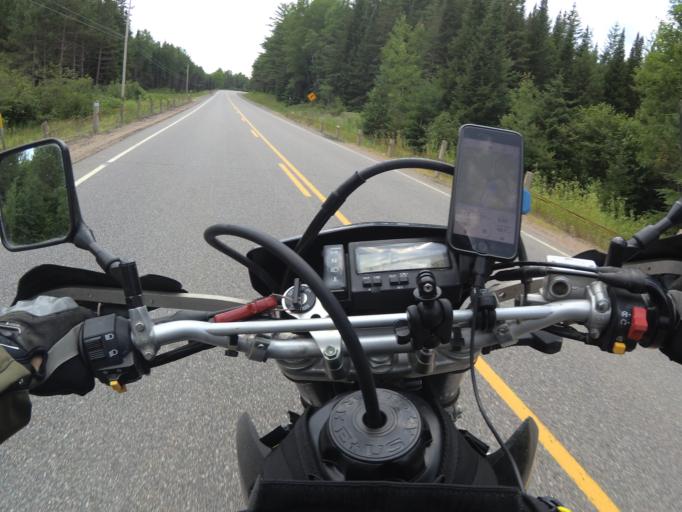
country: CA
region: Ontario
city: Bancroft
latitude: 45.0177
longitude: -77.2675
